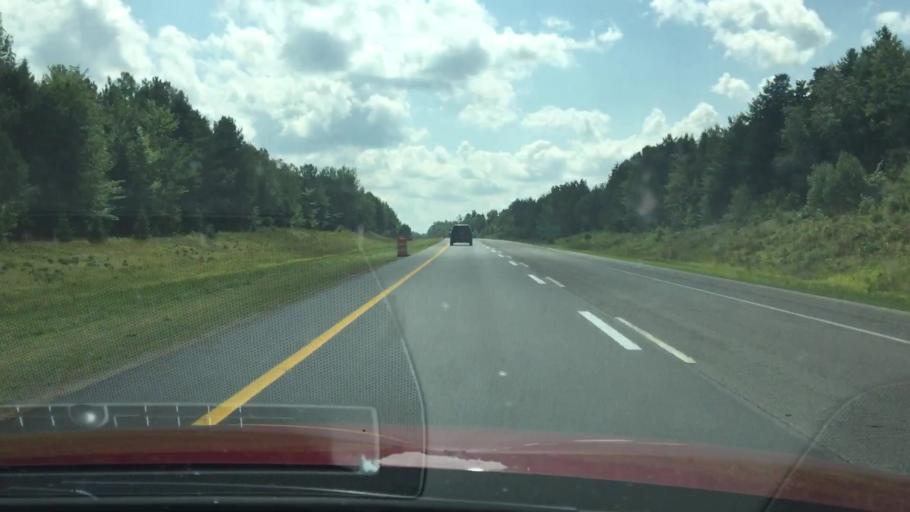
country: US
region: Maine
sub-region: Penobscot County
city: Medway
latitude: 45.6309
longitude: -68.5050
